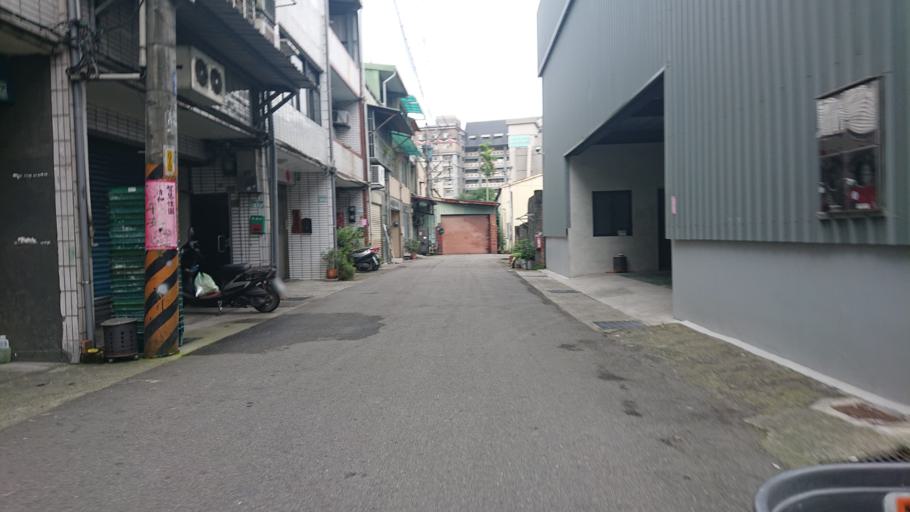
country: TW
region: Taiwan
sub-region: Taoyuan
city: Taoyuan
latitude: 24.9422
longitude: 121.3576
